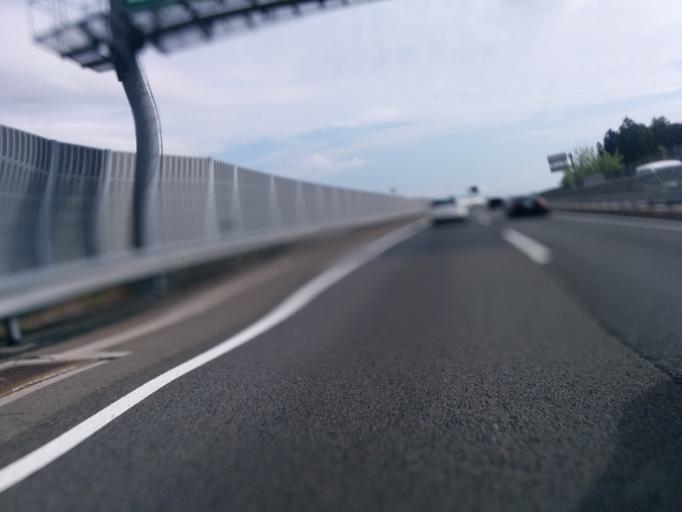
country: JP
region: Mie
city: Komono
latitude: 34.9372
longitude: 136.4898
